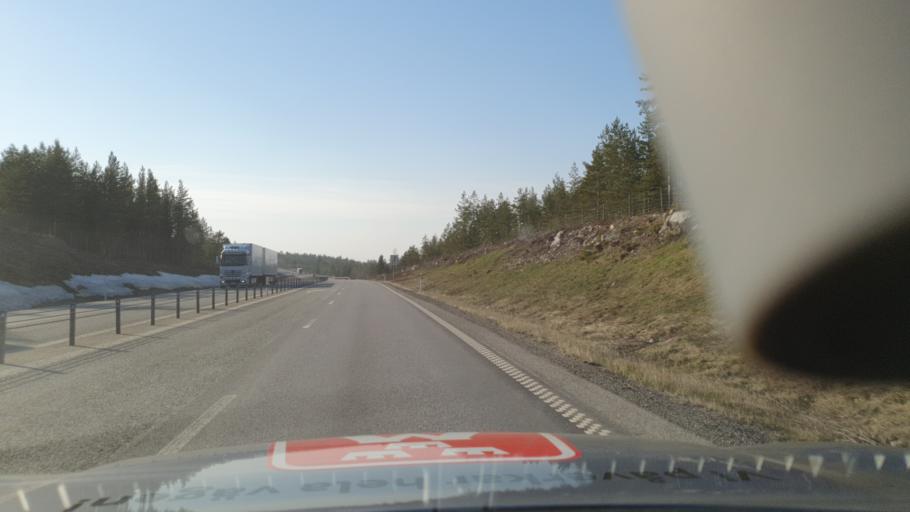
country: SE
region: Vaesterbotten
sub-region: Skelleftea Kommun
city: Soedra Bergsbyn
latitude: 64.6819
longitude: 21.0695
